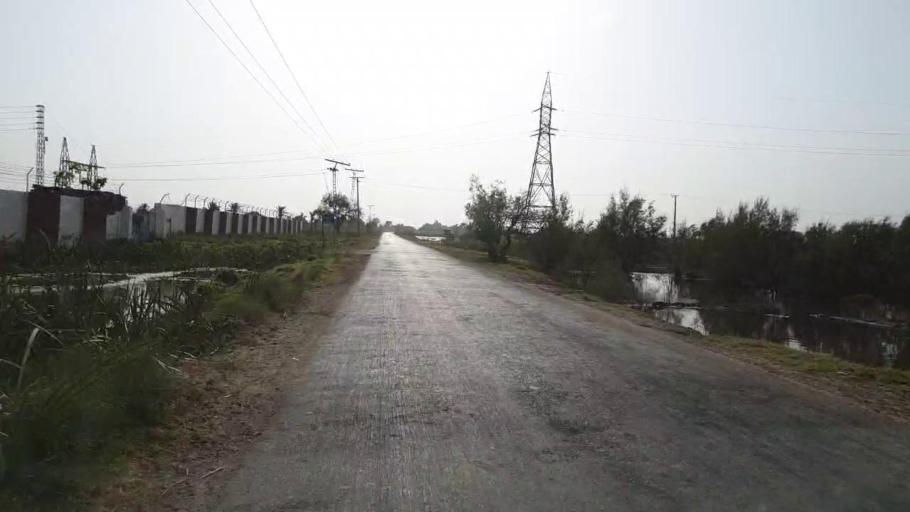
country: PK
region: Sindh
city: Jam Sahib
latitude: 26.3790
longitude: 68.8950
